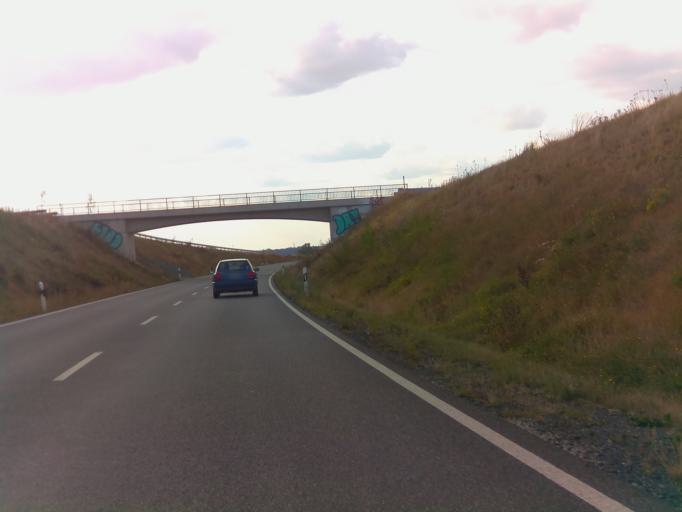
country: DE
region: Hesse
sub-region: Regierungsbezirk Kassel
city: Dipperz
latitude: 50.5364
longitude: 9.7959
